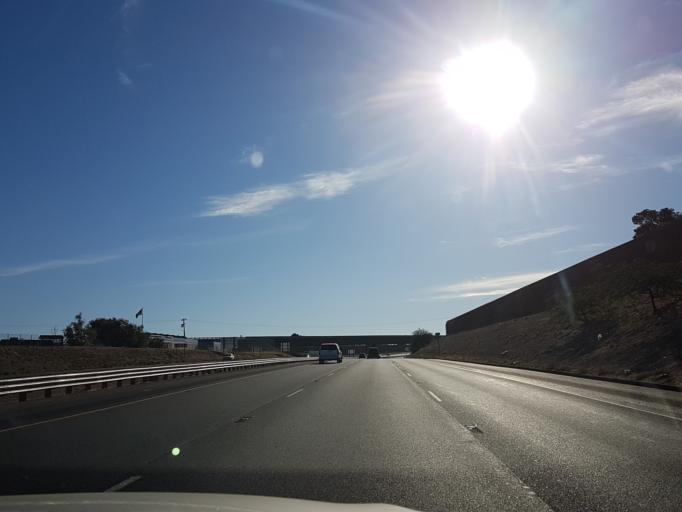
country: US
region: California
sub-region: San Bernardino County
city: Barstow
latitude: 34.8894
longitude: -117.0041
